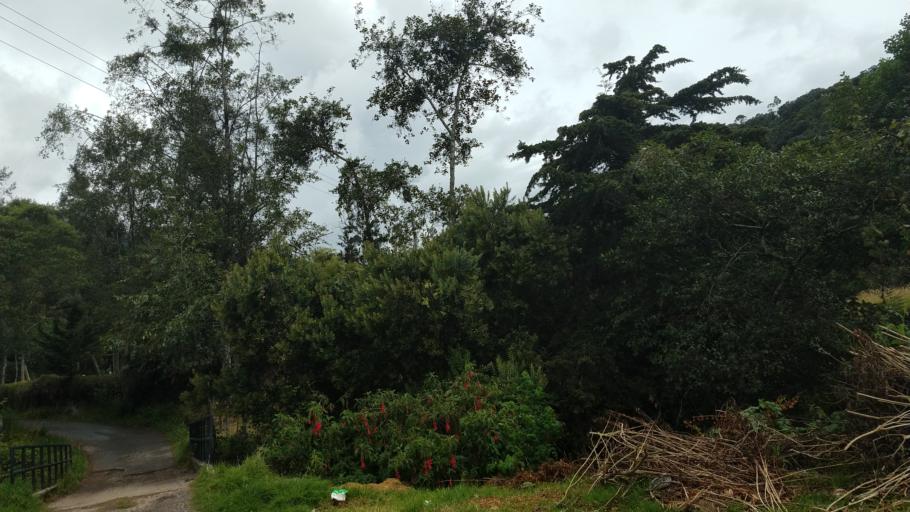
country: CO
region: Boyaca
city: Arcabuco
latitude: 5.7531
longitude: -73.4373
